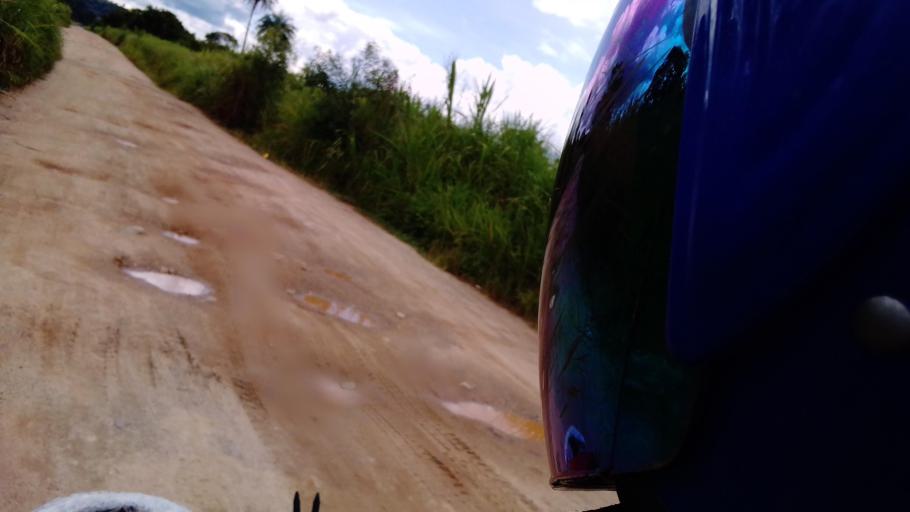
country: SL
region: Eastern Province
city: Koidu
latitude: 8.6737
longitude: -10.9860
